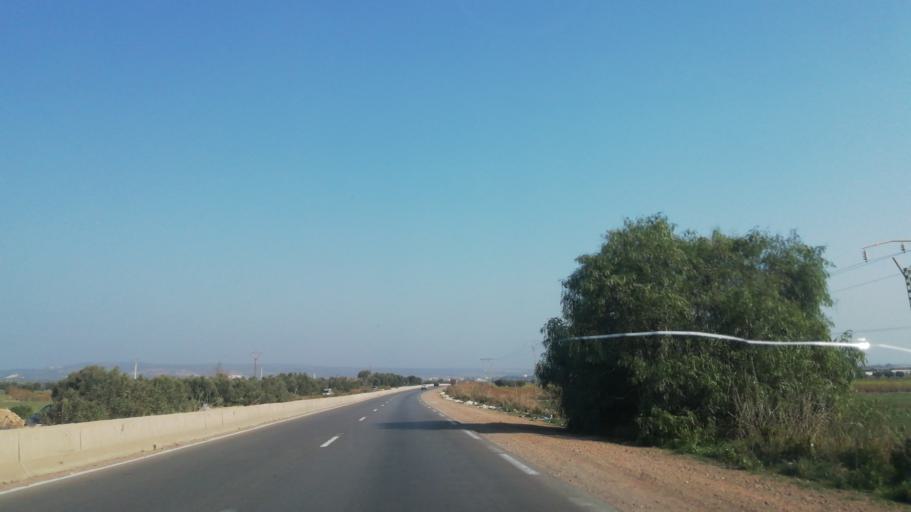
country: DZ
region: Oran
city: Bou Tlelis
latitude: 35.5599
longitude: -0.9313
